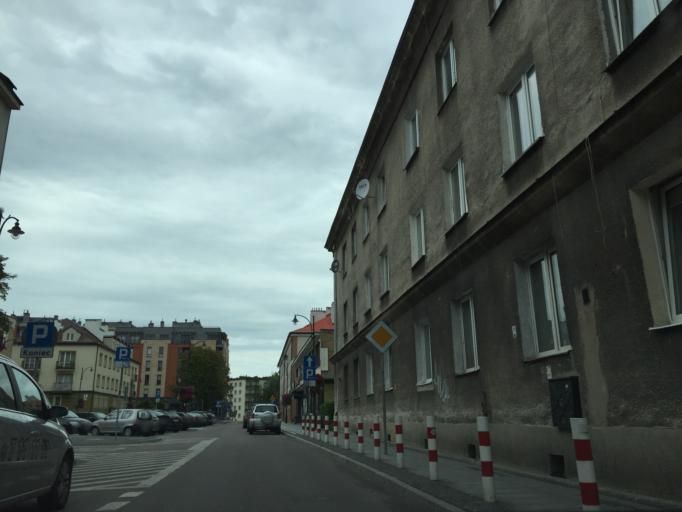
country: PL
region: Podlasie
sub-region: Bialystok
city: Bialystok
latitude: 53.1337
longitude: 23.1562
